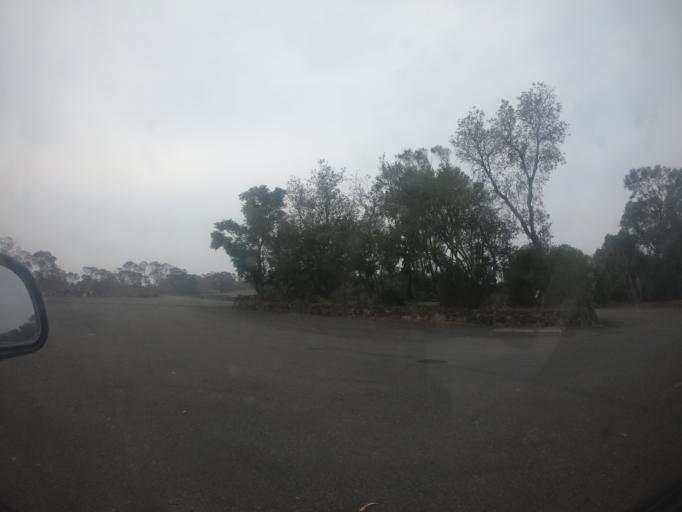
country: AU
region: New South Wales
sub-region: Shellharbour
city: Croom
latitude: -34.6144
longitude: 150.8532
